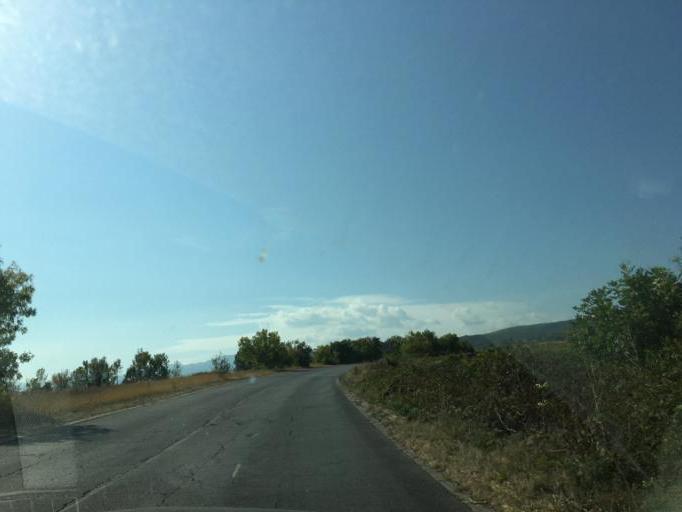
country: BG
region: Pazardzhik
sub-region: Obshtina Peshtera
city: Peshtera
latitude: 42.1140
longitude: 24.2973
